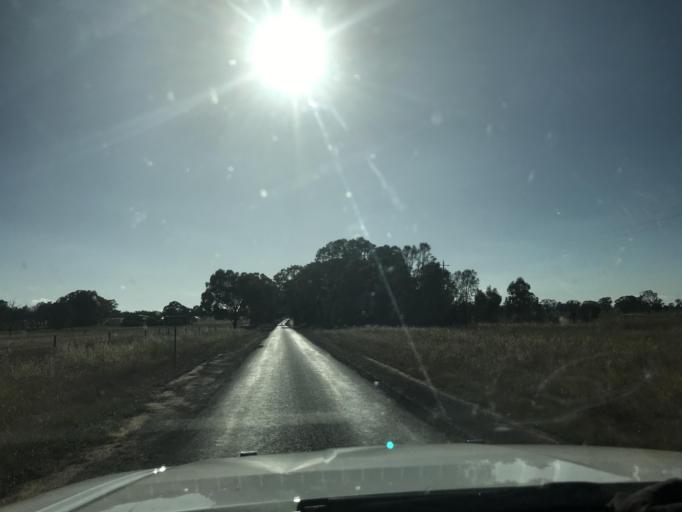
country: AU
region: Victoria
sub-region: Horsham
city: Horsham
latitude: -37.0039
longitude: 141.6087
